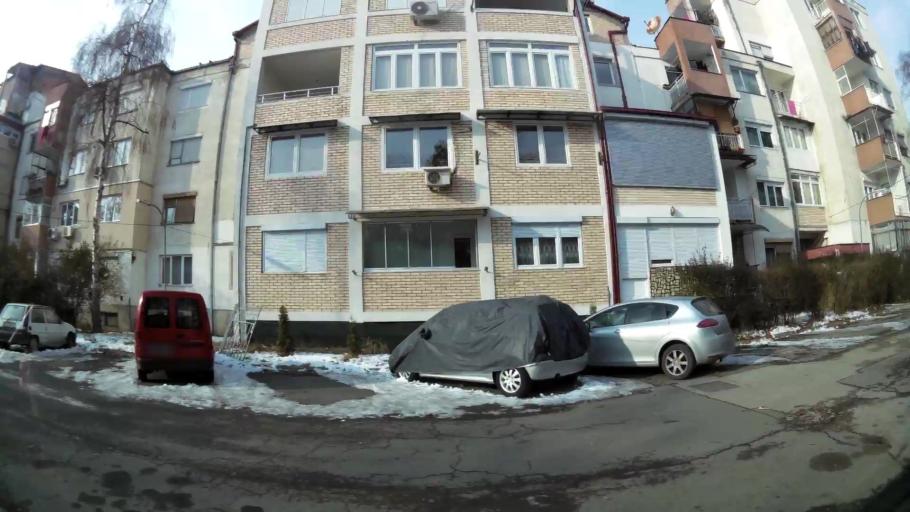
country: MK
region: Cair
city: Cair
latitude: 42.0198
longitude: 21.4324
